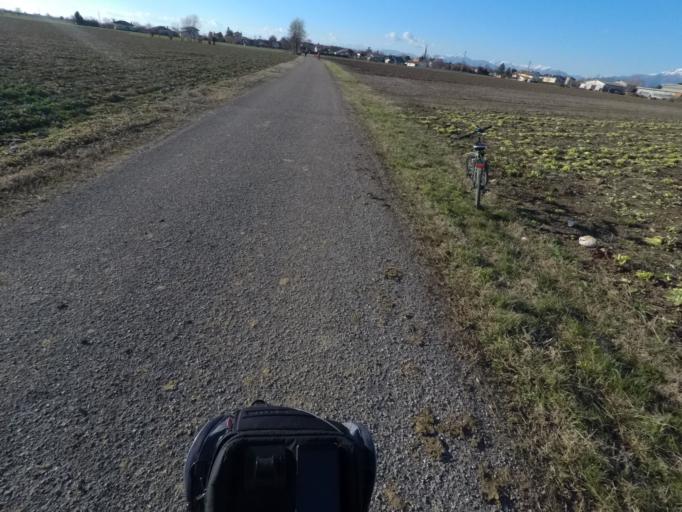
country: IT
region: Friuli Venezia Giulia
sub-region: Provincia di Udine
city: Remanzacco
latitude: 46.1009
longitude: 13.3154
